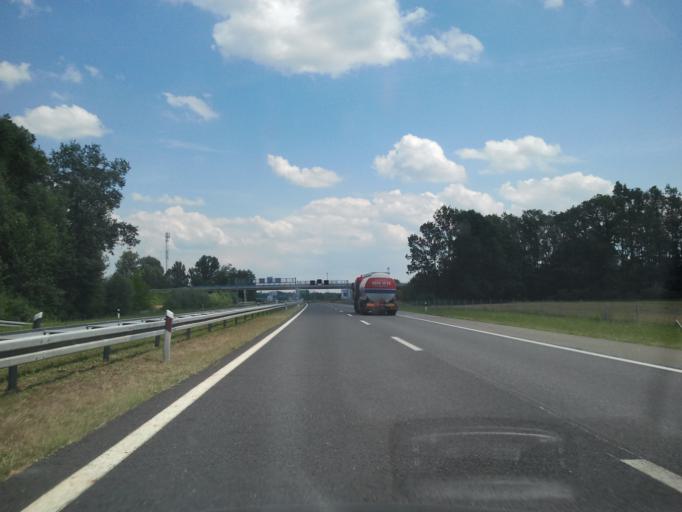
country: HR
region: Brodsko-Posavska
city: Garcin
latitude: 45.1460
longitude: 18.2877
